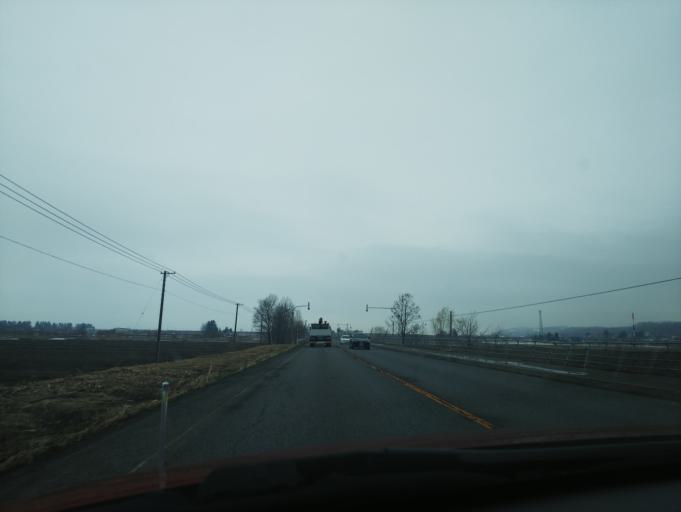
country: JP
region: Hokkaido
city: Nayoro
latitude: 44.0655
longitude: 142.3984
